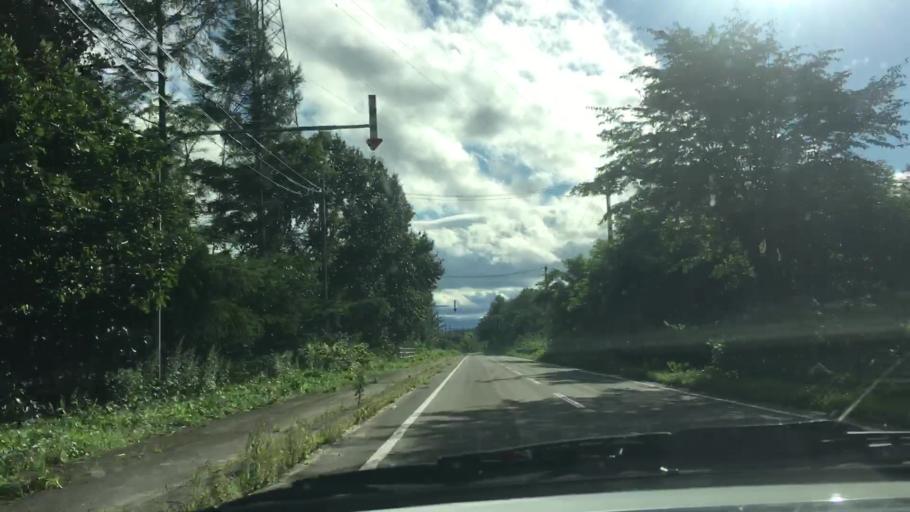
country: JP
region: Hokkaido
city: Otofuke
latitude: 43.1810
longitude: 143.0125
